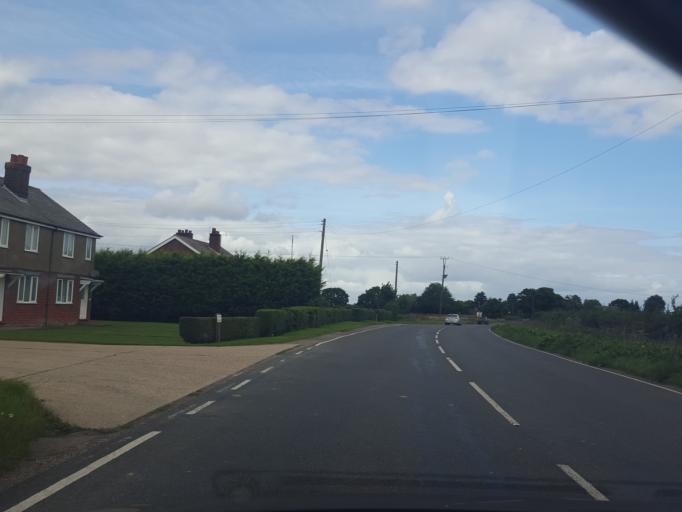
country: GB
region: England
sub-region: Essex
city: Mistley
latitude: 51.9110
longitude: 1.0825
